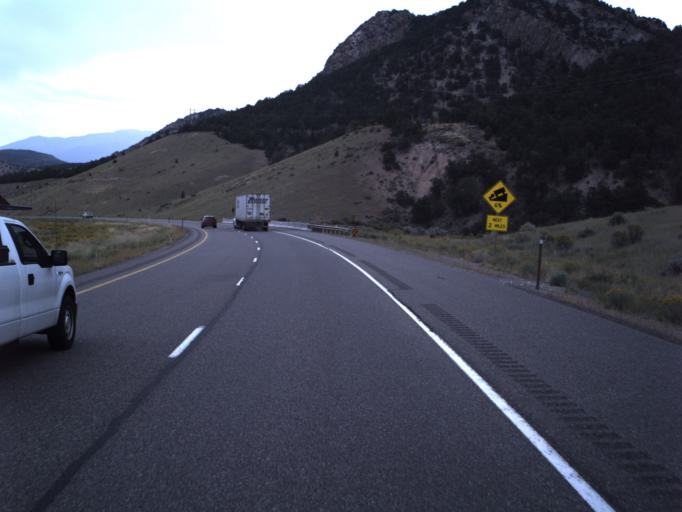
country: US
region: Utah
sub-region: Sevier County
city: Monroe
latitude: 38.5469
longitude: -112.3755
